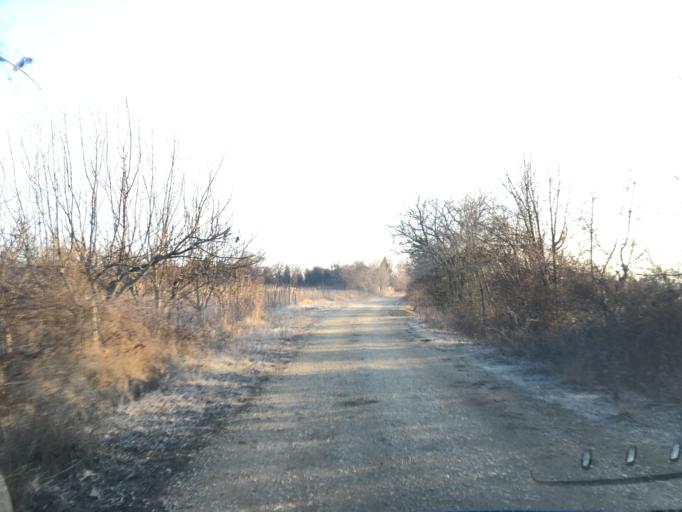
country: GR
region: West Macedonia
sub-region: Nomos Kozanis
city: Kozani
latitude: 40.2809
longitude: 21.7662
